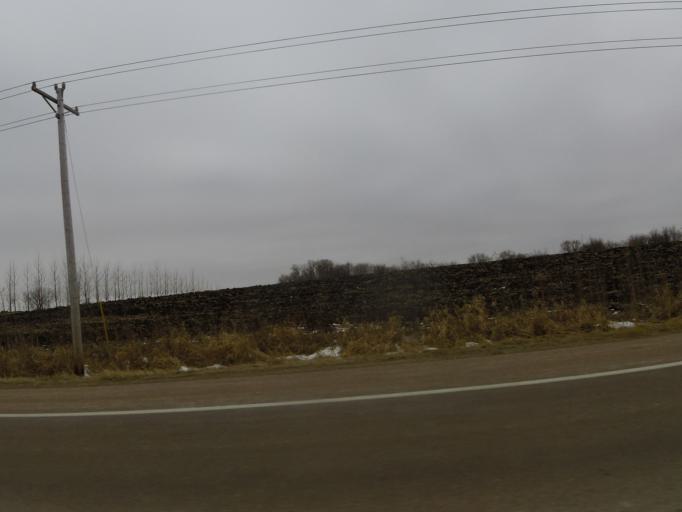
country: US
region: Minnesota
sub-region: Carver County
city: Waconia
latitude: 44.8517
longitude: -93.8192
